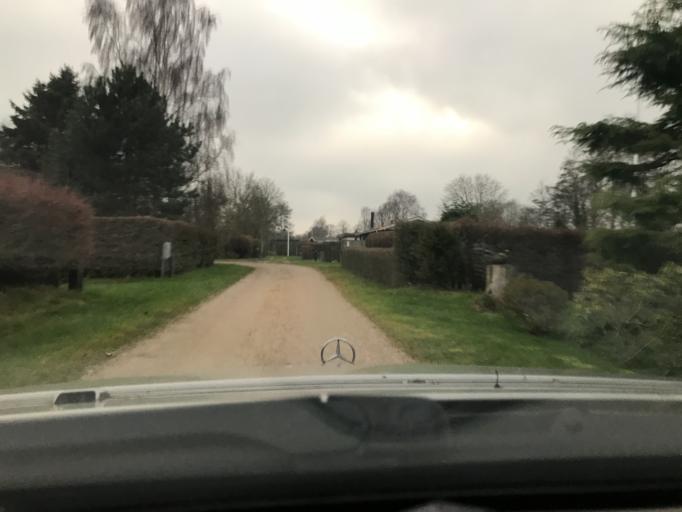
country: DK
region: South Denmark
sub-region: Sonderborg Kommune
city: Horuphav
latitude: 54.8737
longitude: 10.0182
